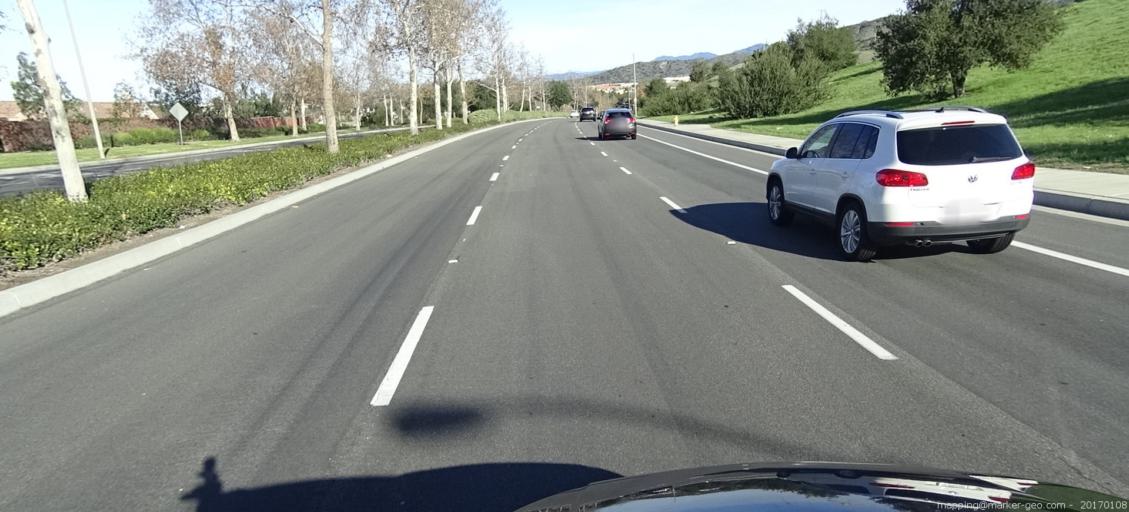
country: US
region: California
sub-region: Orange County
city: Ladera Ranch
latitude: 33.5463
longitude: -117.6292
